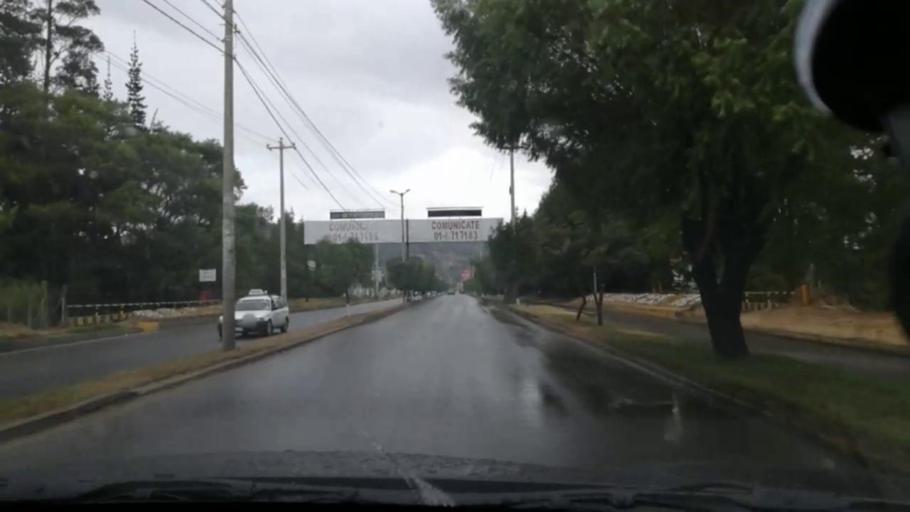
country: PE
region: Cajamarca
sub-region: Provincia de Cajamarca
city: Cajamarca
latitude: -7.1651
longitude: -78.4786
